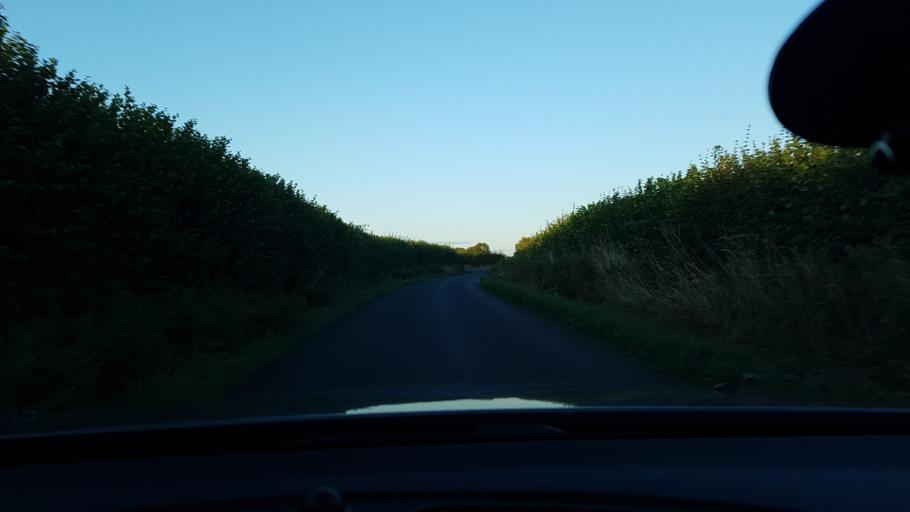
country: GB
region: England
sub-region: West Berkshire
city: Hungerford
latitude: 51.3911
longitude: -1.5272
